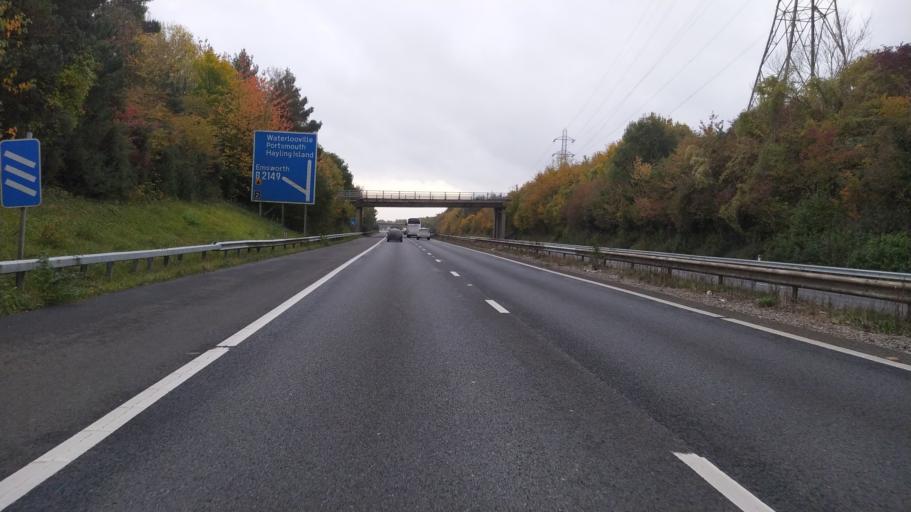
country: GB
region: England
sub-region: Hampshire
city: Cowplain
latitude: 50.9141
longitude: -0.9989
